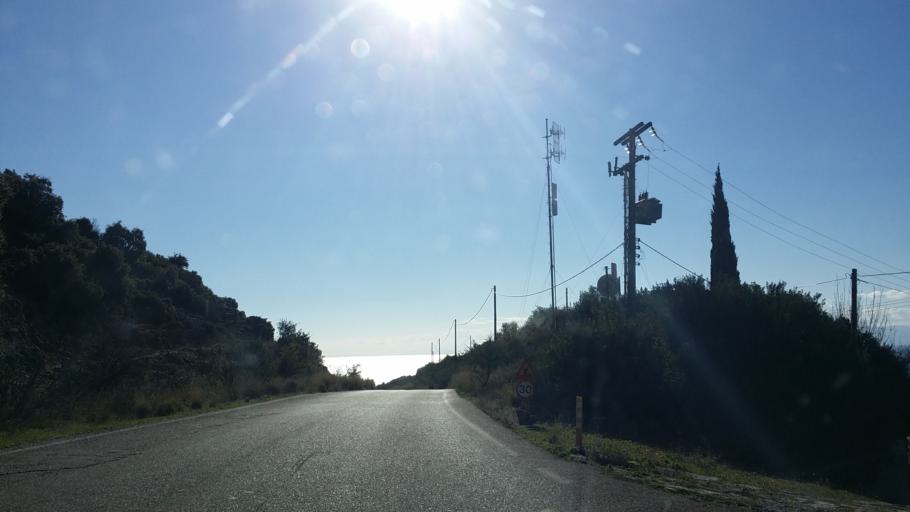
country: GR
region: West Greece
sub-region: Nomos Aitolias kai Akarnanias
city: Archontochorion
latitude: 38.6559
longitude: 20.9923
